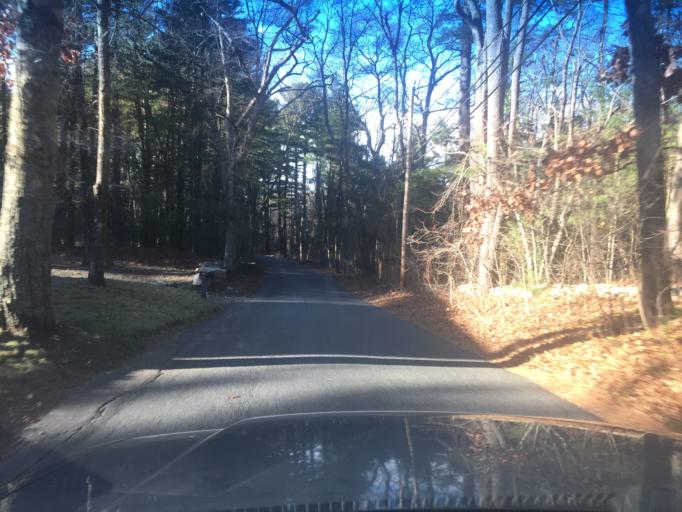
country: US
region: Massachusetts
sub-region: Middlesex County
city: Ashland
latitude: 42.2232
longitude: -71.4693
